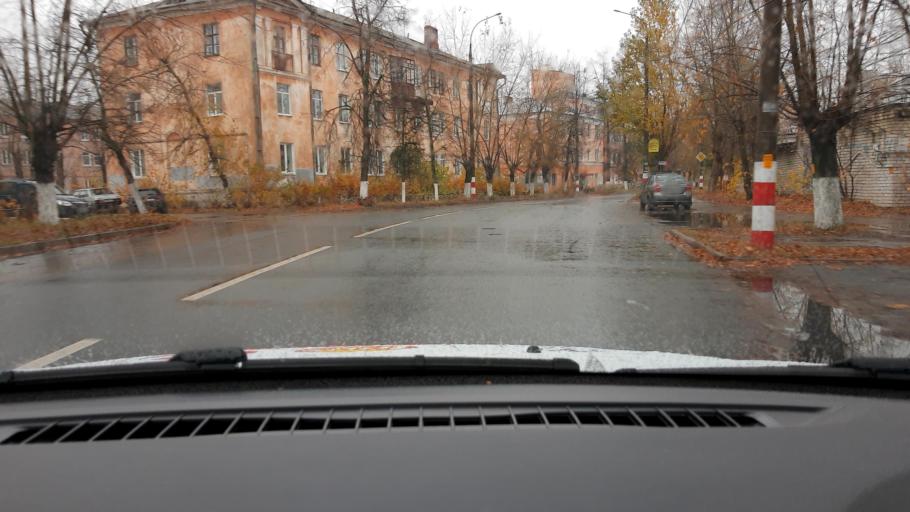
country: RU
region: Nizjnij Novgorod
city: Dzerzhinsk
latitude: 56.2411
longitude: 43.4598
